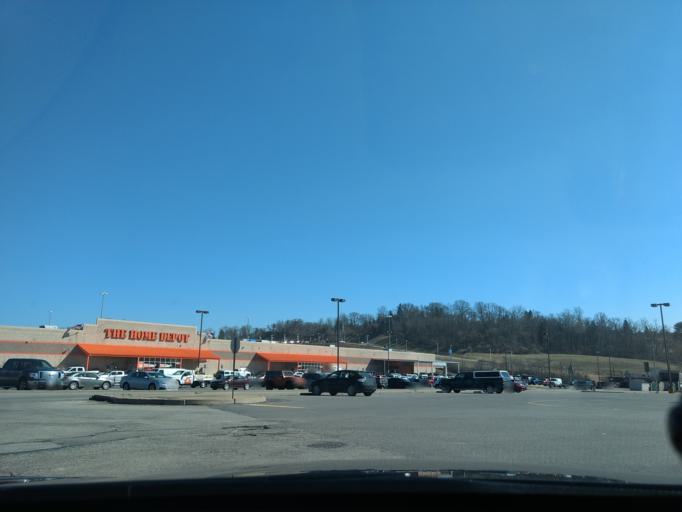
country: US
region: Pennsylvania
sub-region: Washington County
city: East Washington
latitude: 40.1846
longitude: -80.2324
